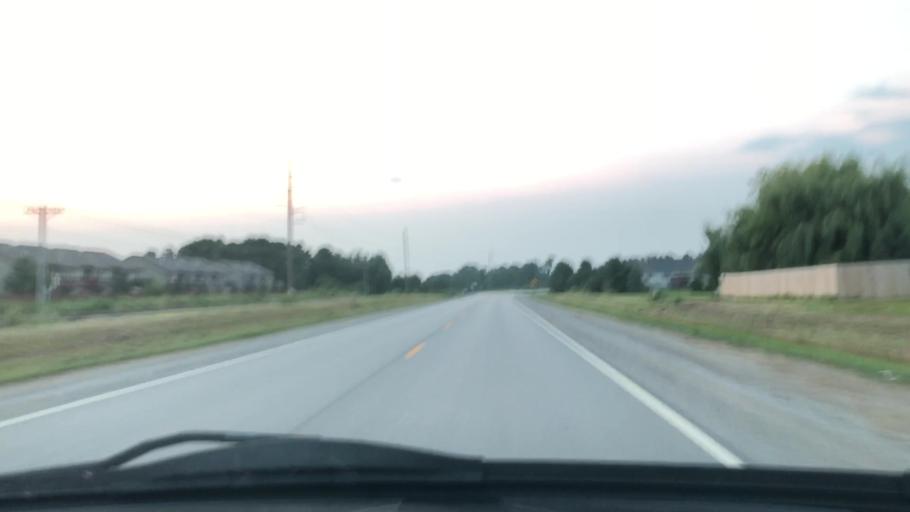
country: US
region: Iowa
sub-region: Johnson County
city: North Liberty
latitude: 41.7640
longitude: -91.6147
